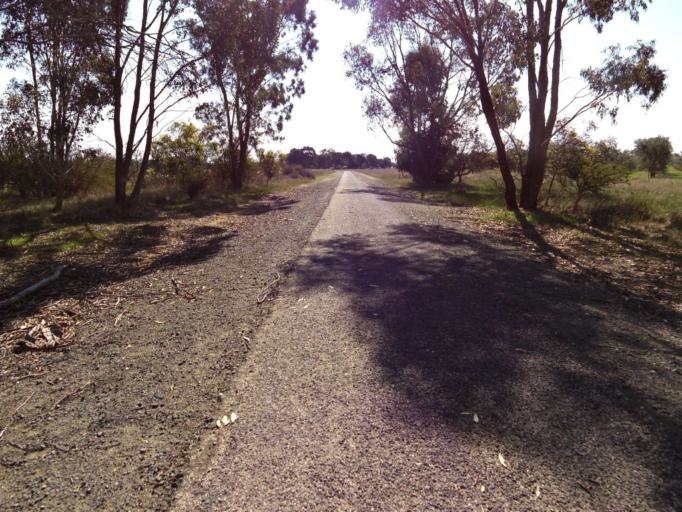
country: AU
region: New South Wales
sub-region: Corowa Shire
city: Corowa
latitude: -36.0408
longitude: 146.4542
